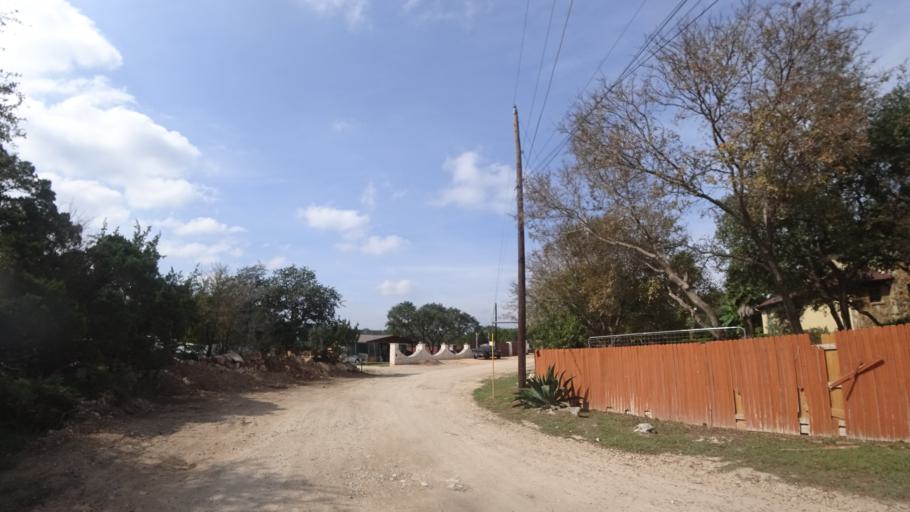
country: US
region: Texas
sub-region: Travis County
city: Hudson Bend
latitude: 30.3858
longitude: -97.9349
